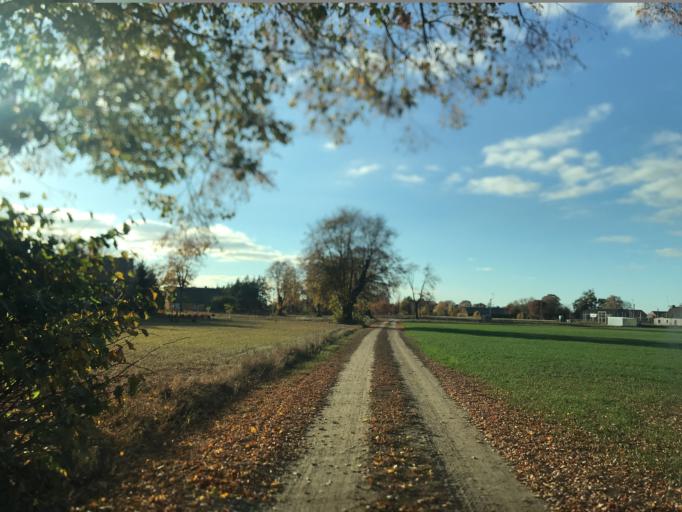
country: PL
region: Warmian-Masurian Voivodeship
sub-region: Powiat dzialdowski
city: Lidzbark
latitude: 53.3632
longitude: 19.7999
